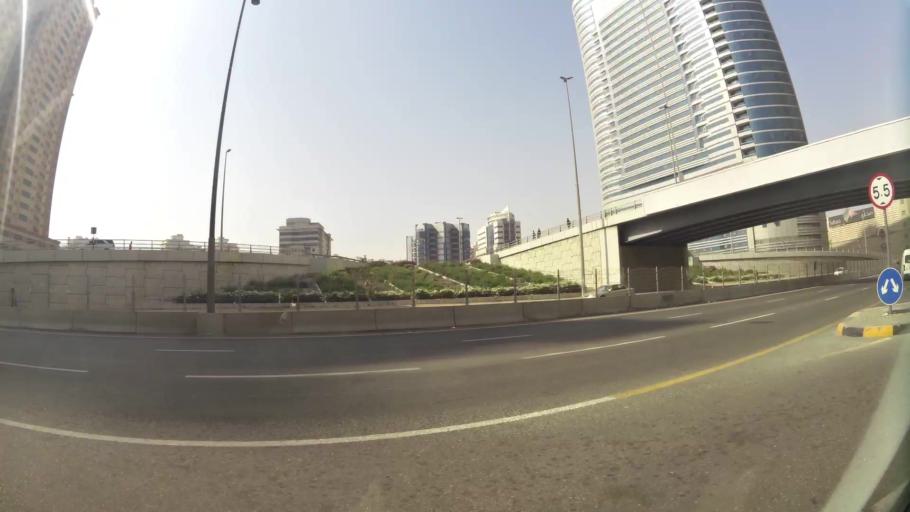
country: AE
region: Ash Shariqah
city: Sharjah
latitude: 25.2998
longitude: 55.3777
